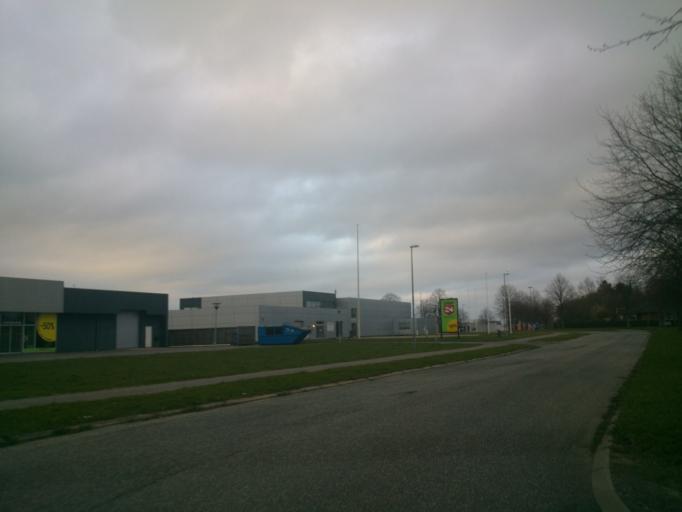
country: DK
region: South Denmark
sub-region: Fredericia Kommune
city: Snoghoj
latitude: 55.5670
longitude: 9.7020
